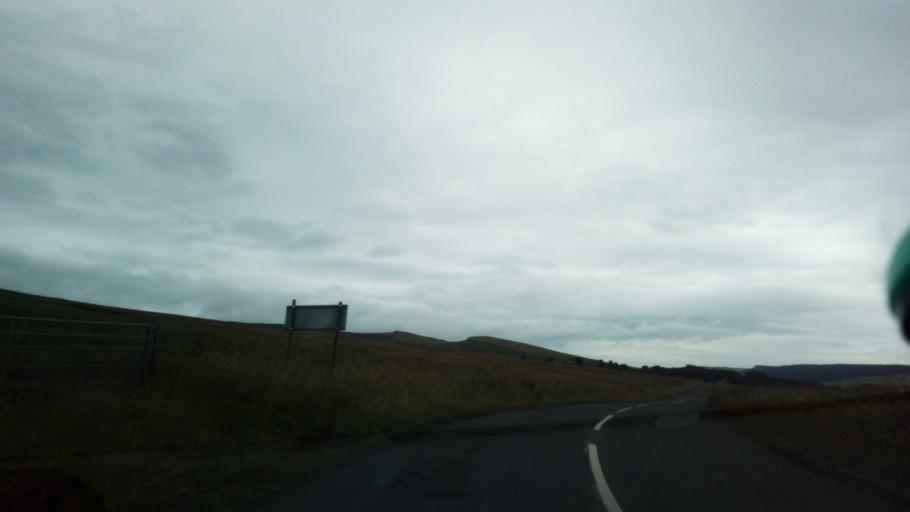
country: GB
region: England
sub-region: County Durham
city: Holwick
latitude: 54.5915
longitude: -2.1764
